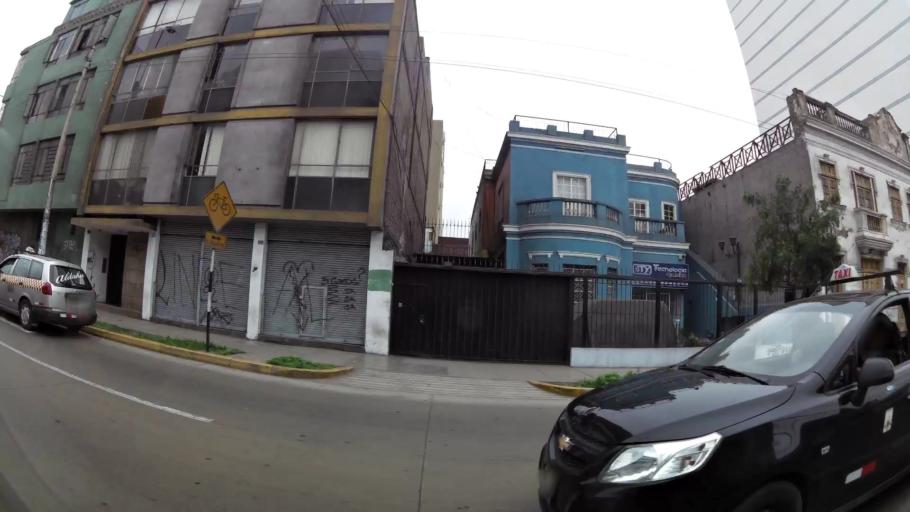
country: PE
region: Lima
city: Lima
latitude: -12.0815
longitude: -77.0337
